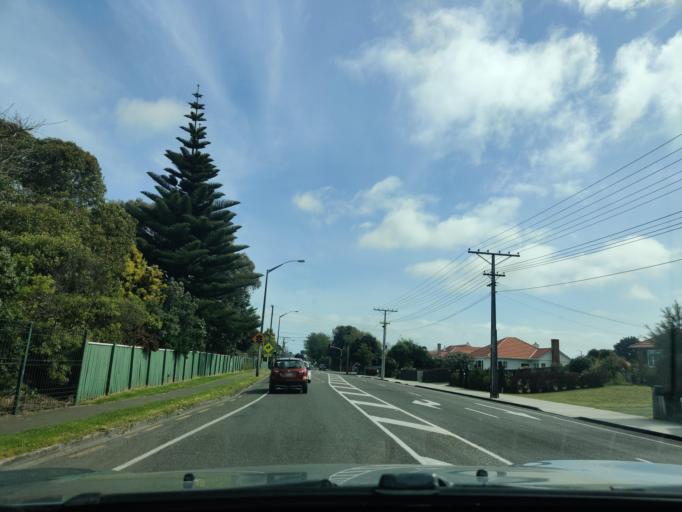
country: NZ
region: Manawatu-Wanganui
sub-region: Wanganui District
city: Wanganui
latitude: -39.9277
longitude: 175.0340
